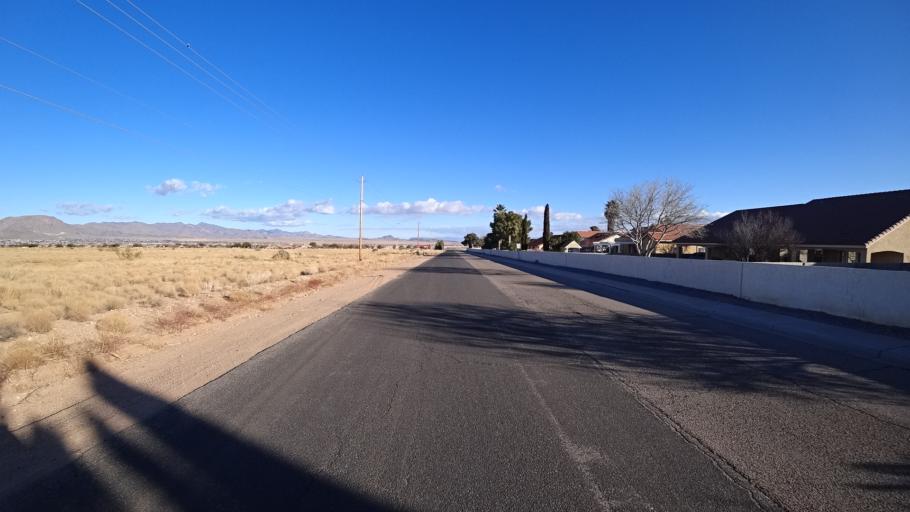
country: US
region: Arizona
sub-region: Mohave County
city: New Kingman-Butler
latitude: 35.2215
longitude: -113.9761
